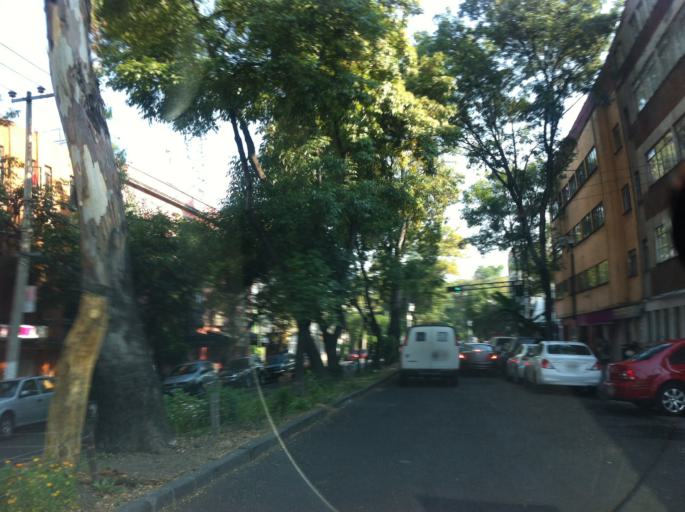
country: MX
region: Mexico City
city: Benito Juarez
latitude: 19.4145
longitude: -99.1587
